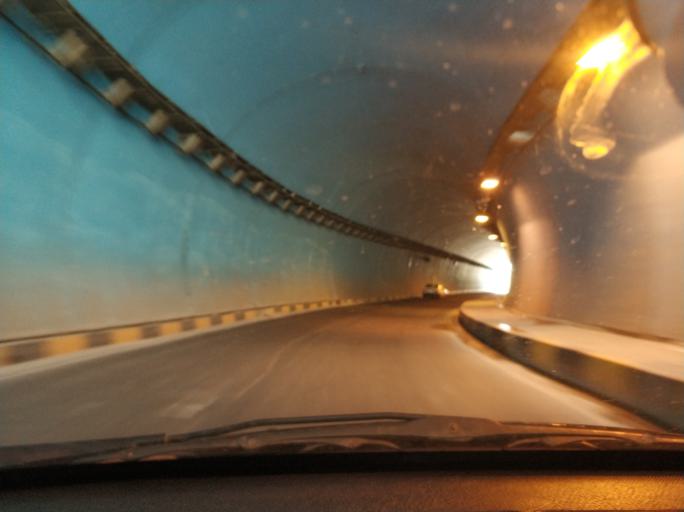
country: IR
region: Tehran
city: Tehran
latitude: 35.7440
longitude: 51.3799
